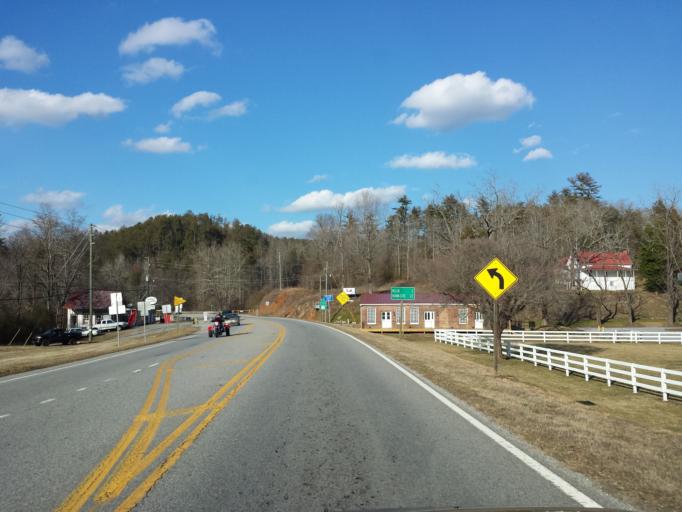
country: US
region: Georgia
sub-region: White County
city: Cleveland
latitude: 34.6857
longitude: -83.7106
